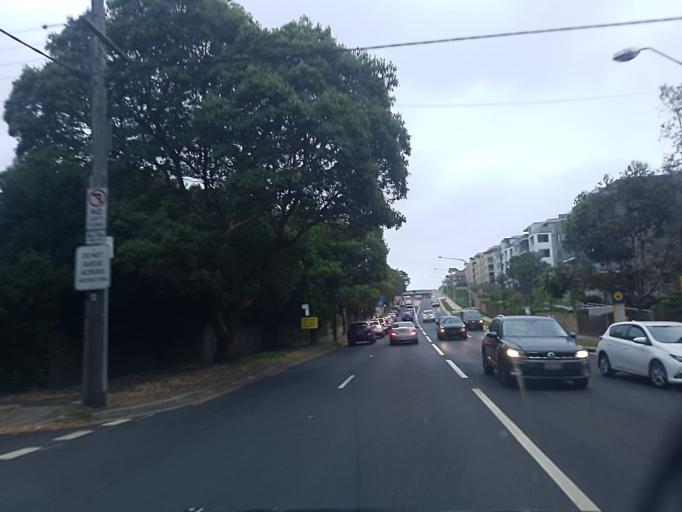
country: AU
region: New South Wales
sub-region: Willoughby
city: Chatswood
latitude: -33.7861
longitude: 151.1837
